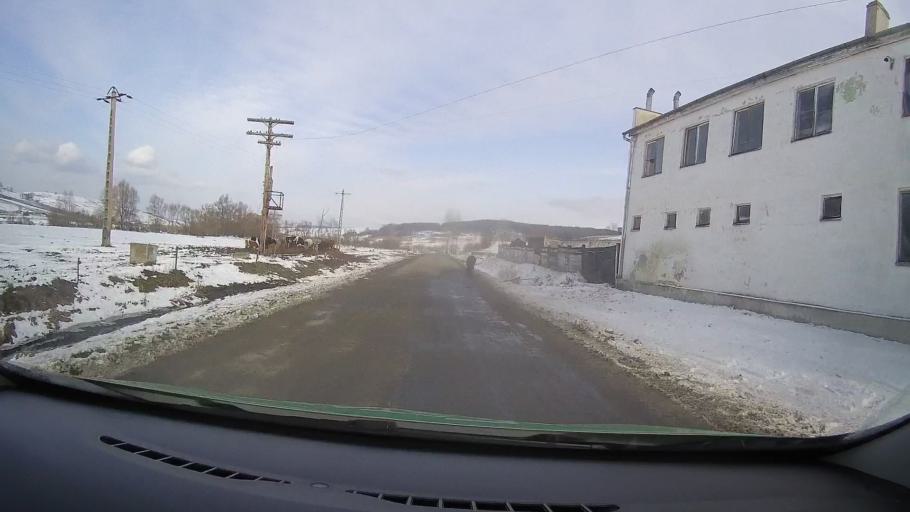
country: RO
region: Sibiu
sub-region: Oras Agnita
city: Ruja
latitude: 45.9835
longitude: 24.6526
